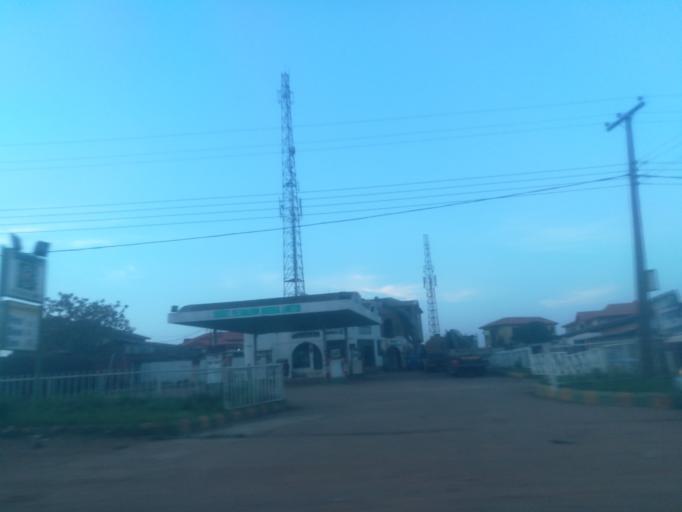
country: NG
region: Ogun
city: Abeokuta
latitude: 7.1765
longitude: 3.3879
